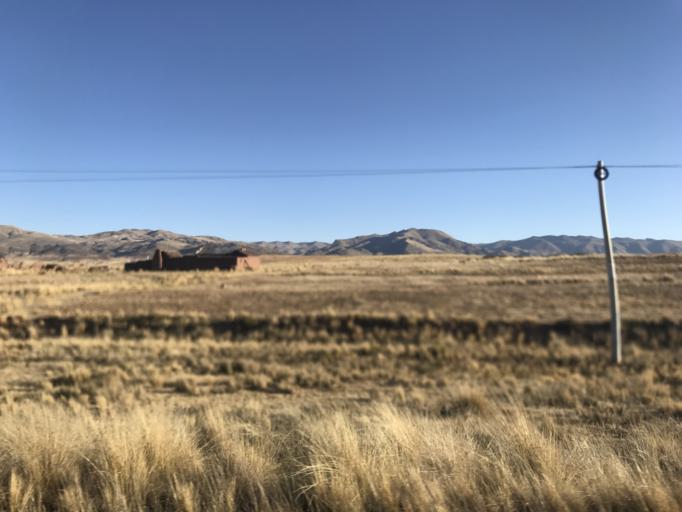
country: BO
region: La Paz
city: Tiahuanaco
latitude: -16.5638
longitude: -68.6224
